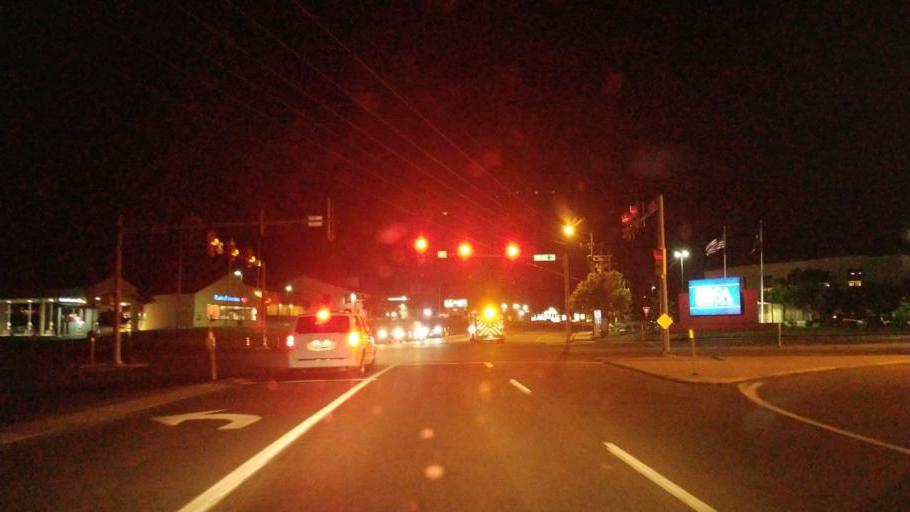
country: US
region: Texas
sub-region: Potter County
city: Amarillo
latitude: 35.1943
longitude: -101.9216
